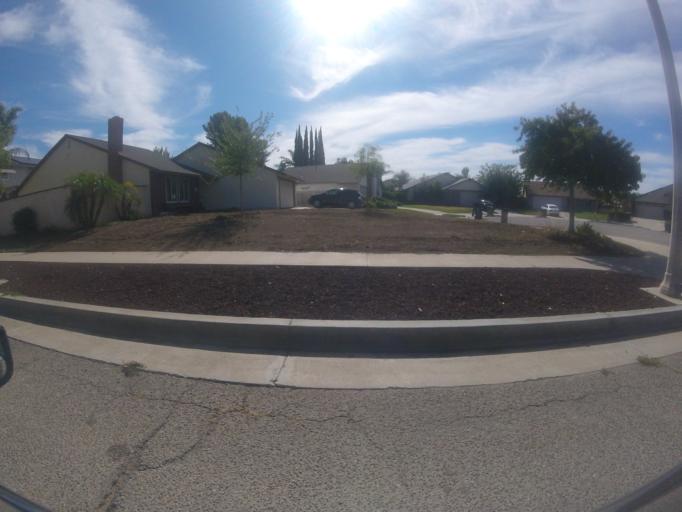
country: US
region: California
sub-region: San Bernardino County
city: Mentone
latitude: 34.0596
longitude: -117.1503
